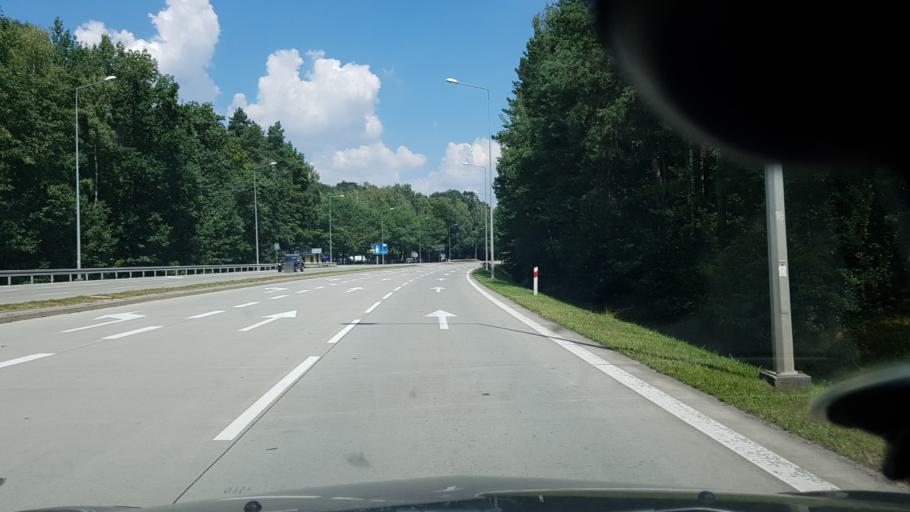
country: PL
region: Silesian Voivodeship
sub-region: Zory
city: Zory
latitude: 50.0609
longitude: 18.7231
